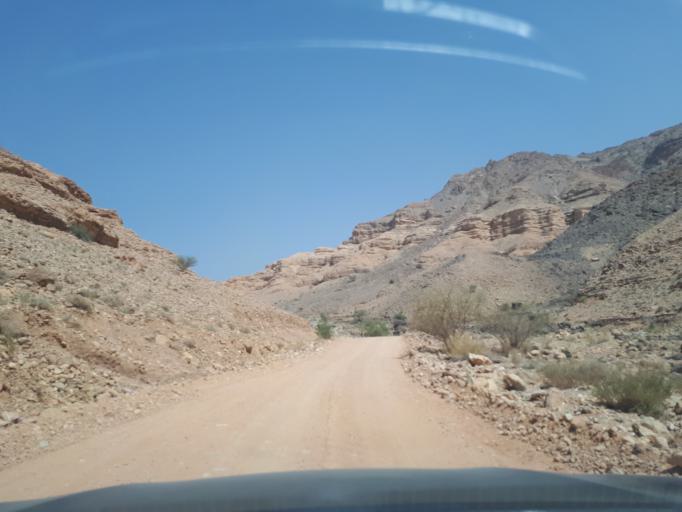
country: OM
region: Ash Sharqiyah
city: Ibra'
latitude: 23.0747
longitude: 58.8806
